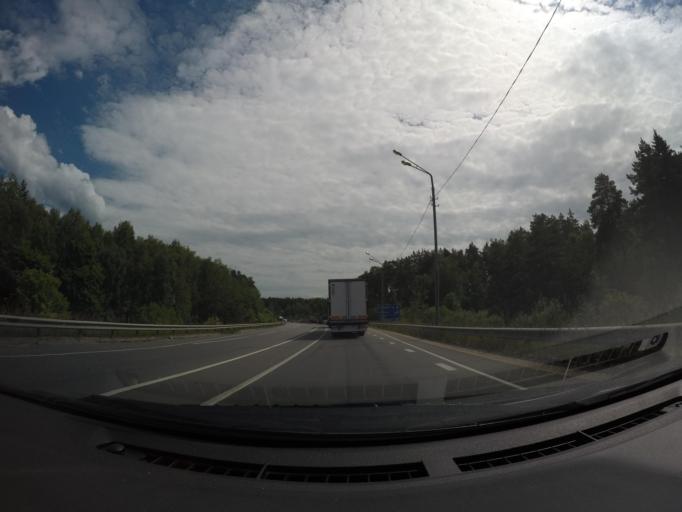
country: RU
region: Moskovskaya
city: Kratovo
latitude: 55.6370
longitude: 38.1862
